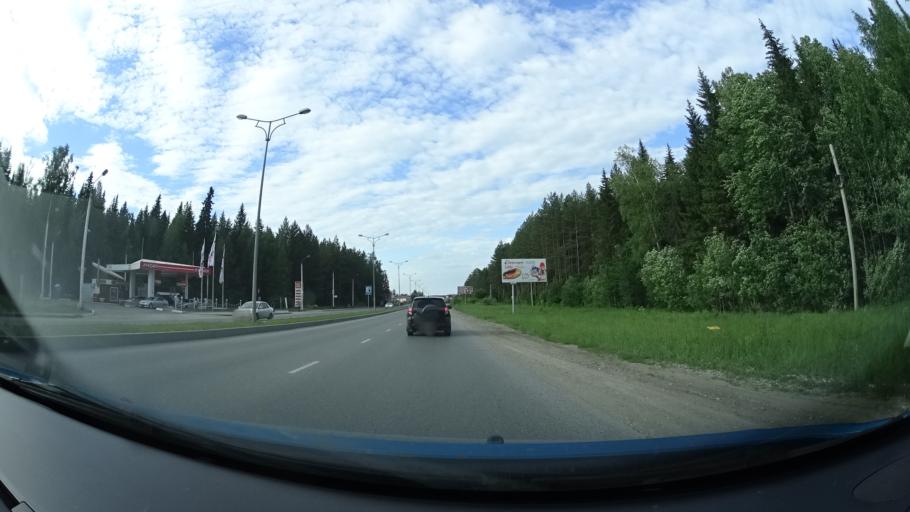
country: RU
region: Perm
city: Kondratovo
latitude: 58.0227
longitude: 55.9951
